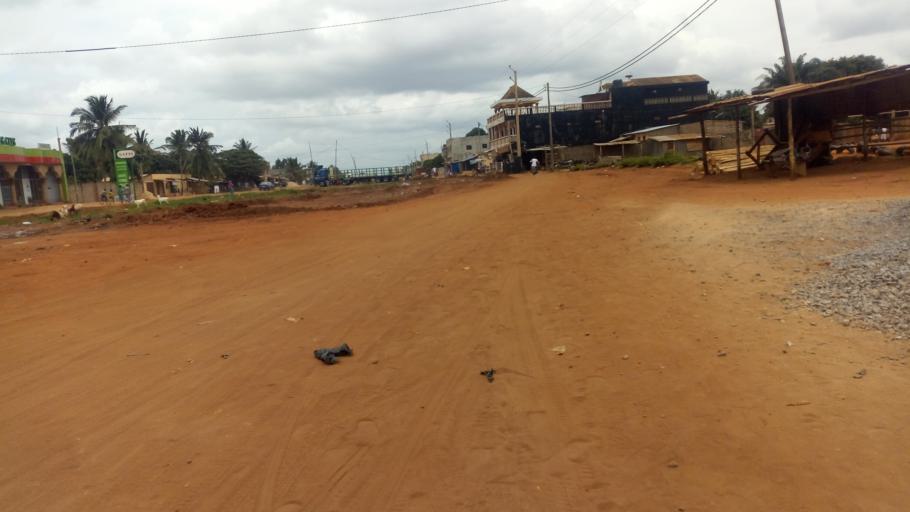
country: TG
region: Maritime
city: Lome
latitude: 6.2343
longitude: 1.1820
